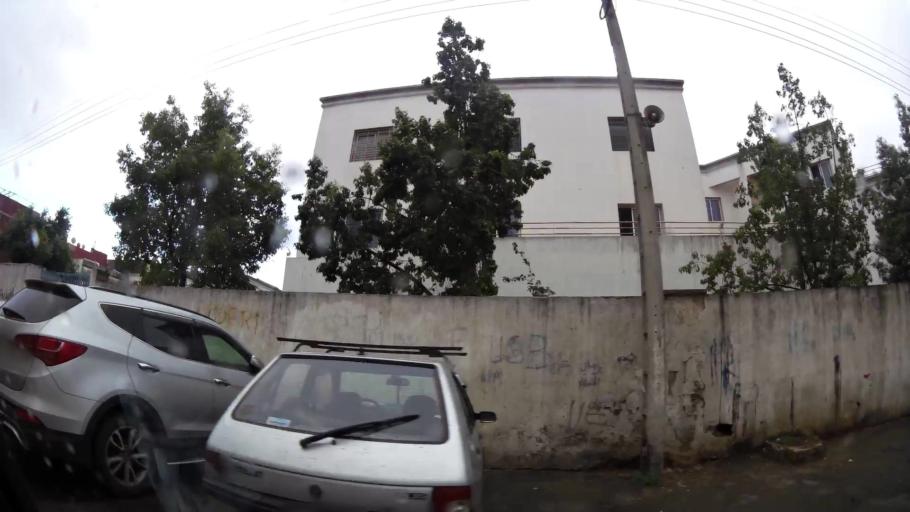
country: MA
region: Grand Casablanca
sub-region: Casablanca
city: Casablanca
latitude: 33.5525
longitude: -7.5778
